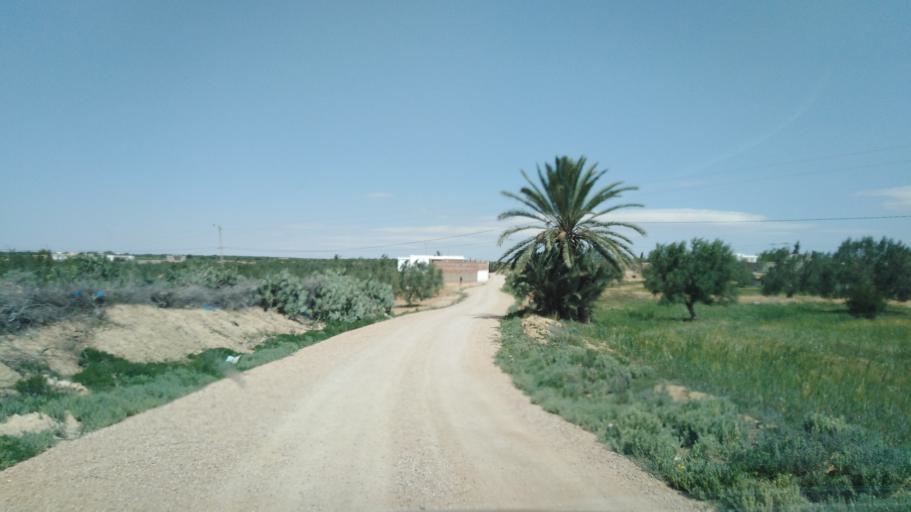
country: TN
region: Safaqis
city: Sfax
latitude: 34.7612
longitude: 10.5246
